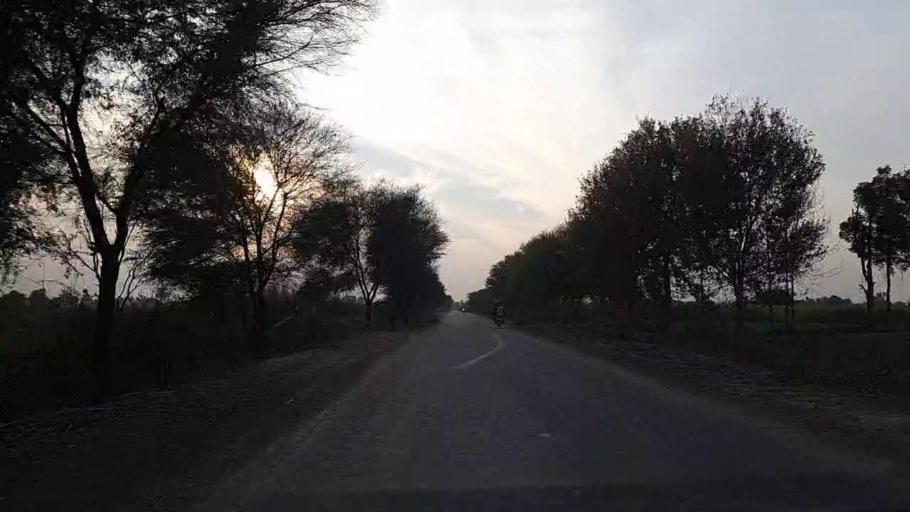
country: PK
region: Sindh
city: Daur
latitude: 26.3980
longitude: 68.4551
